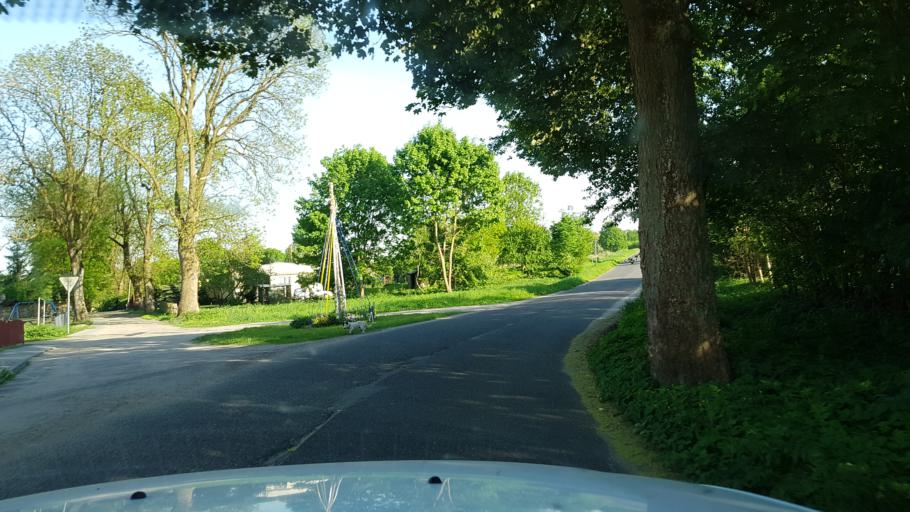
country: PL
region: West Pomeranian Voivodeship
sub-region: Powiat lobeski
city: Radowo Male
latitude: 53.6477
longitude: 15.3714
